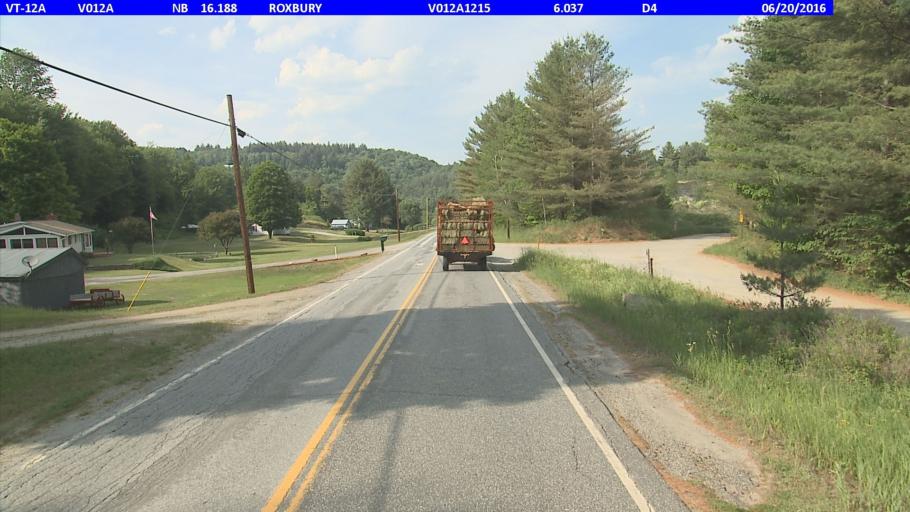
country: US
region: Vermont
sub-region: Washington County
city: Northfield
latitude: 44.1116
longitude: -72.7261
